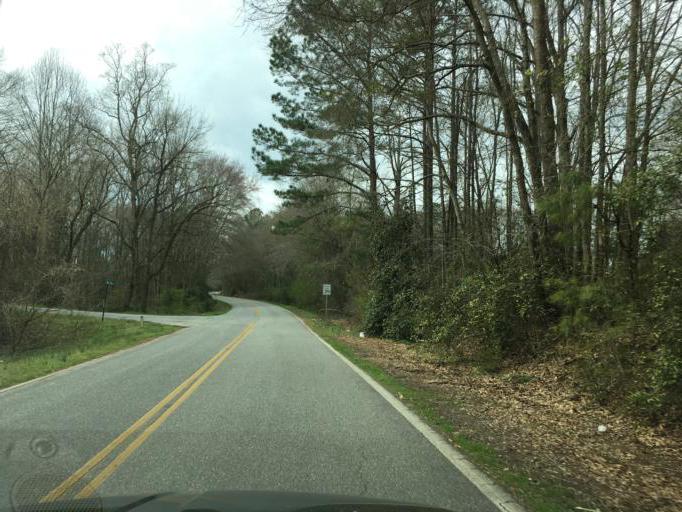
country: US
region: South Carolina
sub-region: Anderson County
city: Pendleton
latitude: 34.6586
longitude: -82.7813
